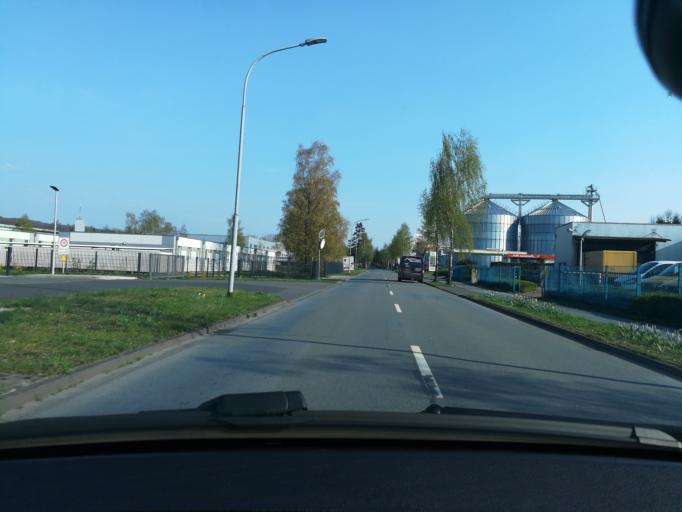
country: DE
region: North Rhine-Westphalia
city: Halle
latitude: 52.0444
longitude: 8.3787
